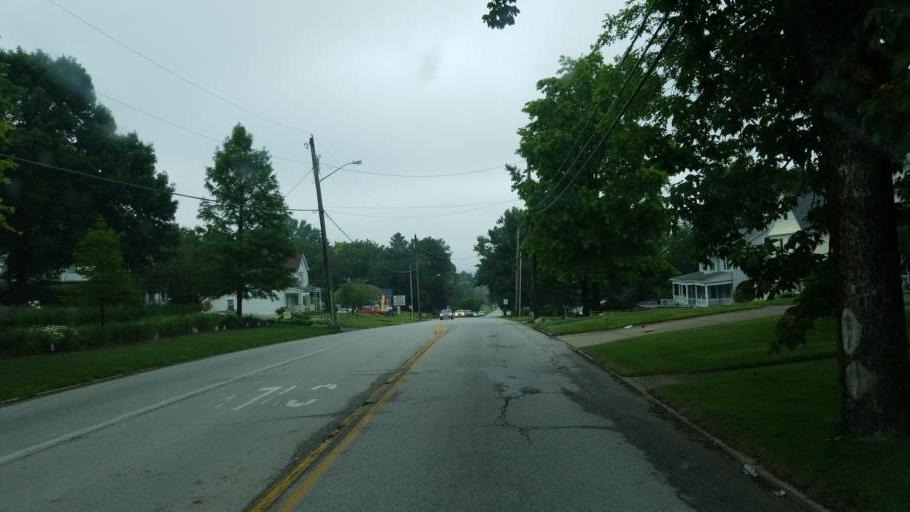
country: US
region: Ohio
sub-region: Highland County
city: Hillsboro
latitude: 39.2093
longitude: -83.6097
